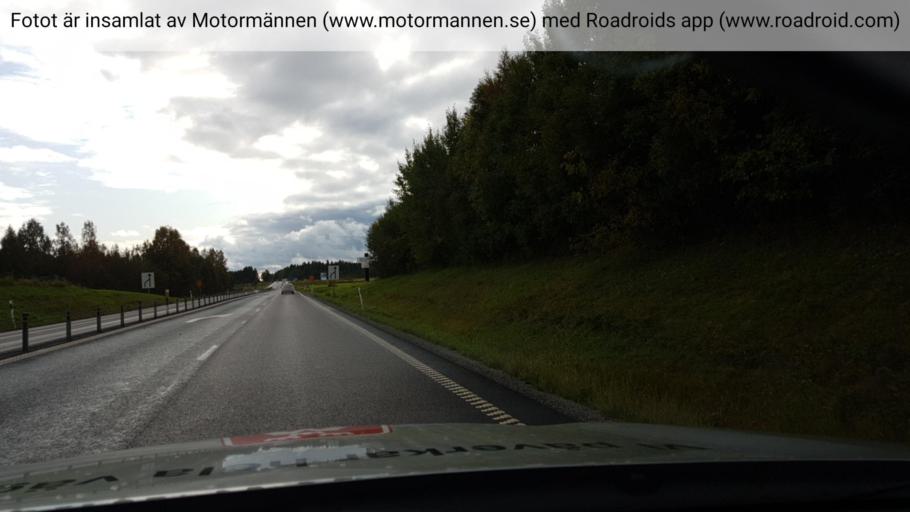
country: SE
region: Norrbotten
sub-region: Bodens Kommun
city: Saevast
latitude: 65.7603
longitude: 21.7631
